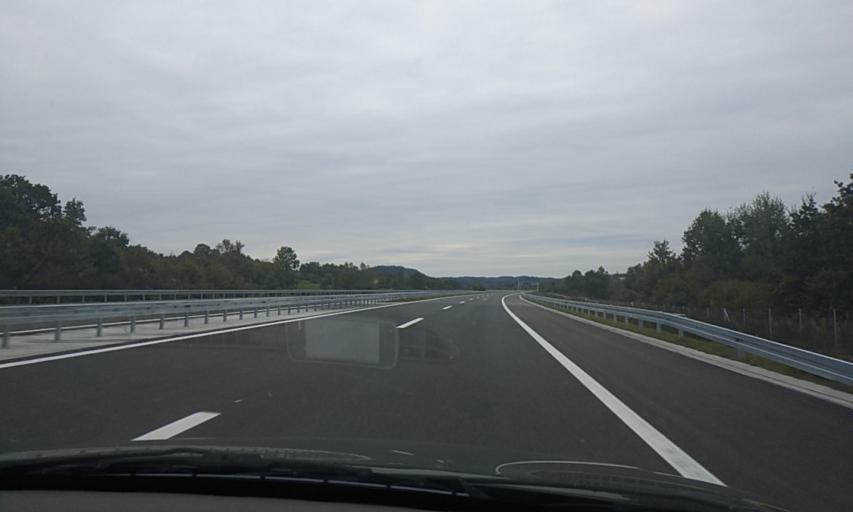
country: BA
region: Republika Srpska
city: Prnjavor
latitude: 44.8782
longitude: 17.6239
